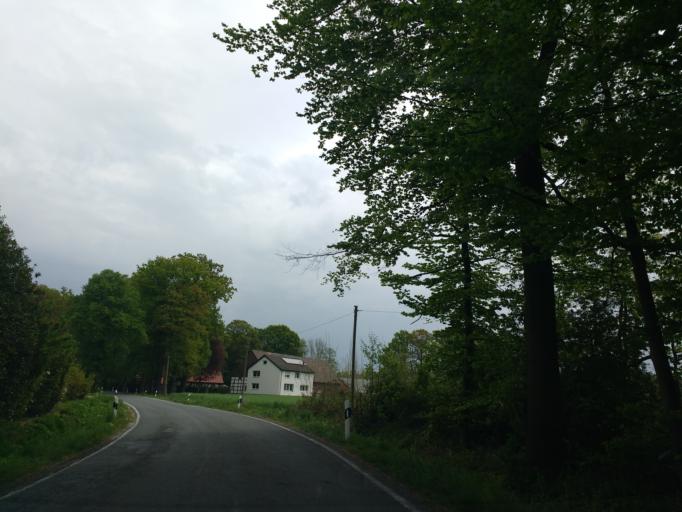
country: DE
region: North Rhine-Westphalia
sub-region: Regierungsbezirk Detmold
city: Delbruck
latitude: 51.8242
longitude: 8.5530
